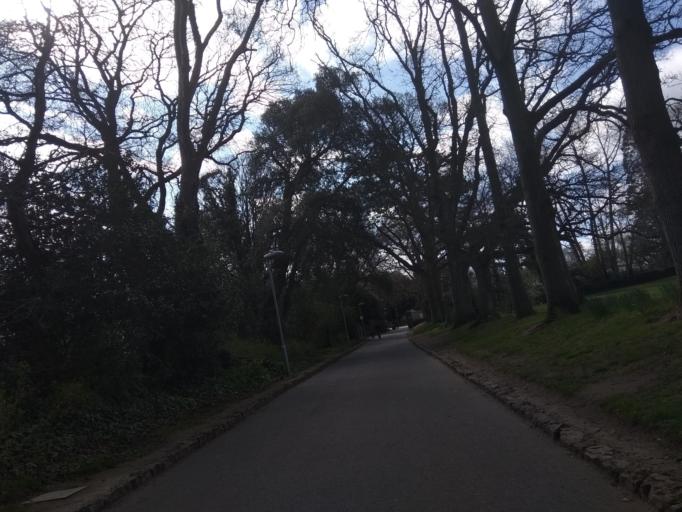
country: IE
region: Leinster
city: Malahide
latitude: 53.4478
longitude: -6.1587
